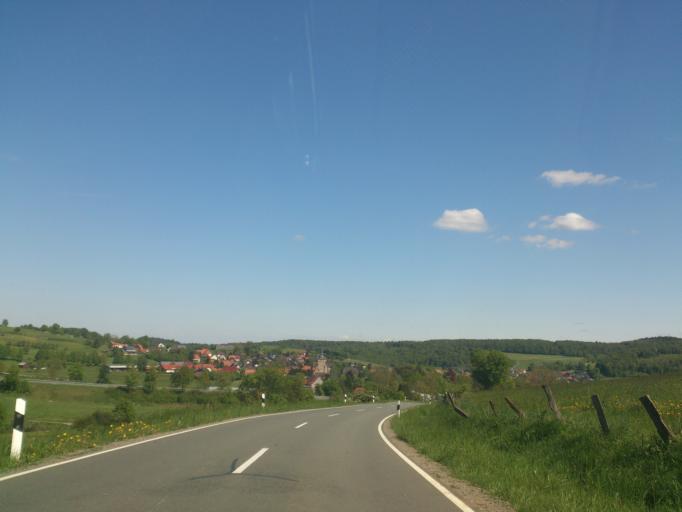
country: DE
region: North Rhine-Westphalia
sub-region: Regierungsbezirk Detmold
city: Bad Driburg
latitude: 51.6768
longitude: 8.9834
